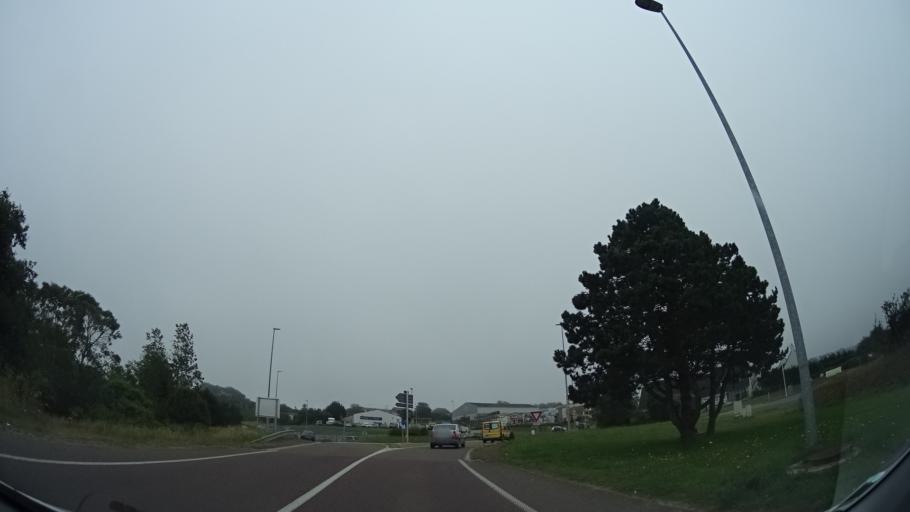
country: FR
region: Lower Normandy
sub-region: Departement de la Manche
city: Les Pieux
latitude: 49.5184
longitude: -1.8125
